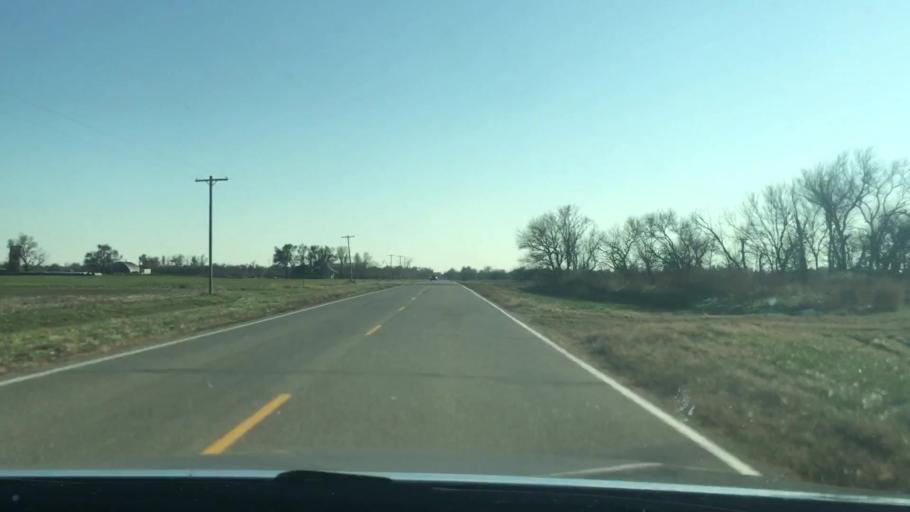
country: US
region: Kansas
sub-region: Reno County
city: Nickerson
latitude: 38.1675
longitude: -98.0876
